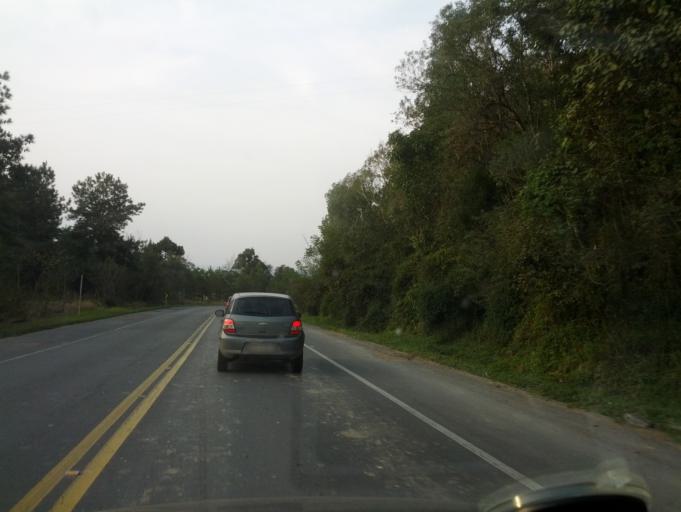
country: BR
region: Santa Catarina
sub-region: Otacilio Costa
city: Otacilio Costa
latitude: -27.2827
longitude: -50.0704
